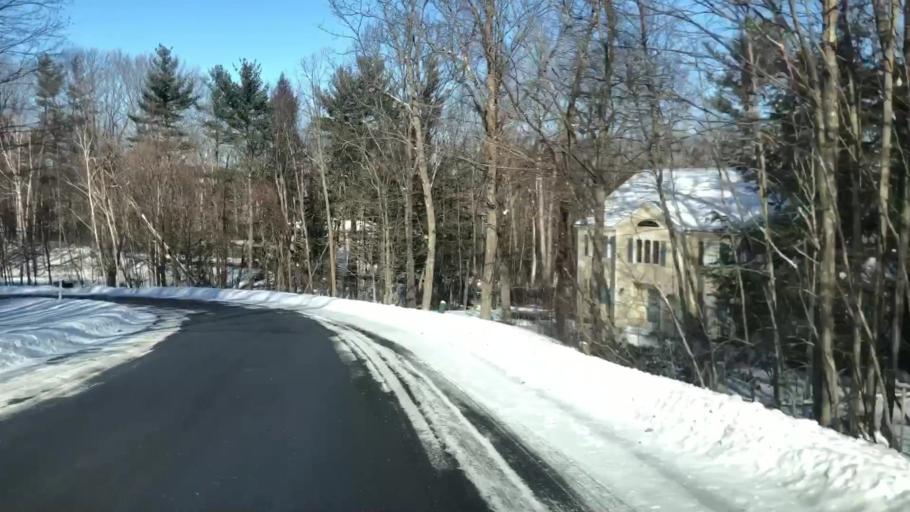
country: US
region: New Hampshire
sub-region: Hillsborough County
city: Bedford
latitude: 42.9434
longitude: -71.5476
